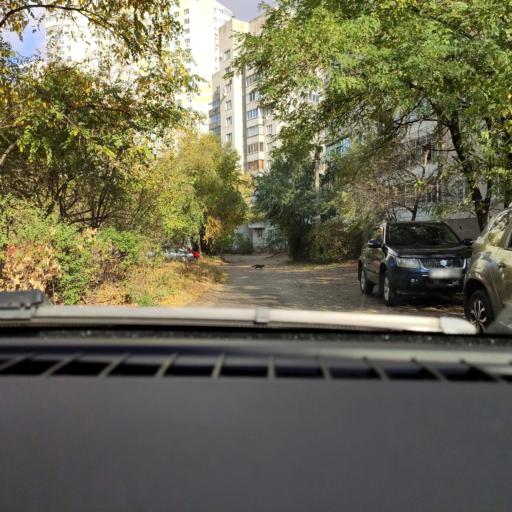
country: RU
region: Voronezj
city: Voronezh
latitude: 51.6805
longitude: 39.2511
